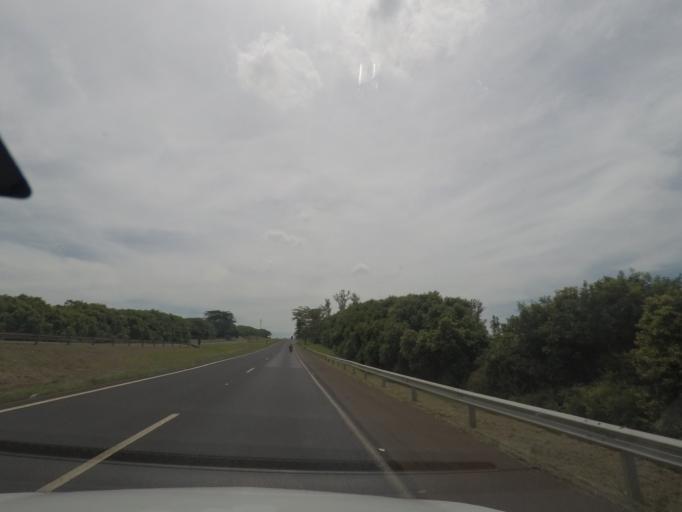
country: BR
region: Sao Paulo
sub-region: Bebedouro
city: Bebedouro
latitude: -20.9982
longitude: -48.4312
